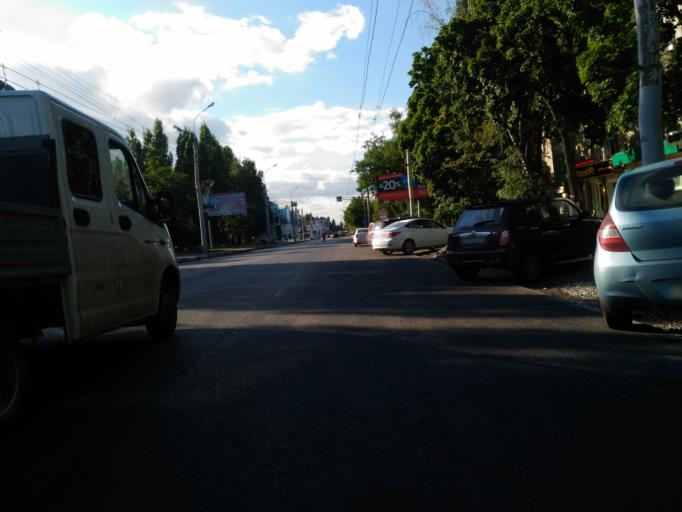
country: RU
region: Voronezj
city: Voronezh
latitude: 51.6505
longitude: 39.1523
